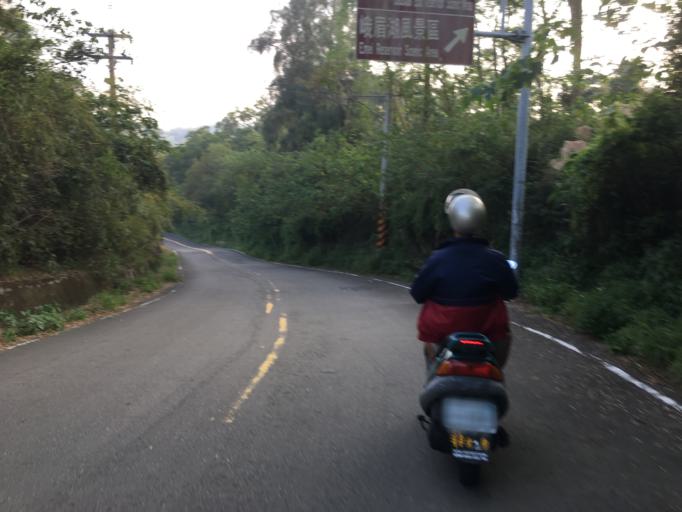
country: TW
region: Taiwan
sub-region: Hsinchu
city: Hsinchu
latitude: 24.7362
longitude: 121.0264
